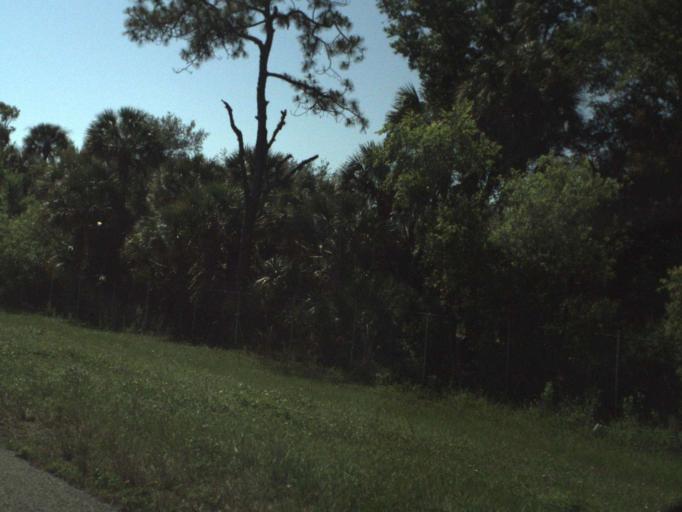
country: US
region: Florida
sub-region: Brevard County
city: Cocoa West
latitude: 28.3709
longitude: -80.8955
